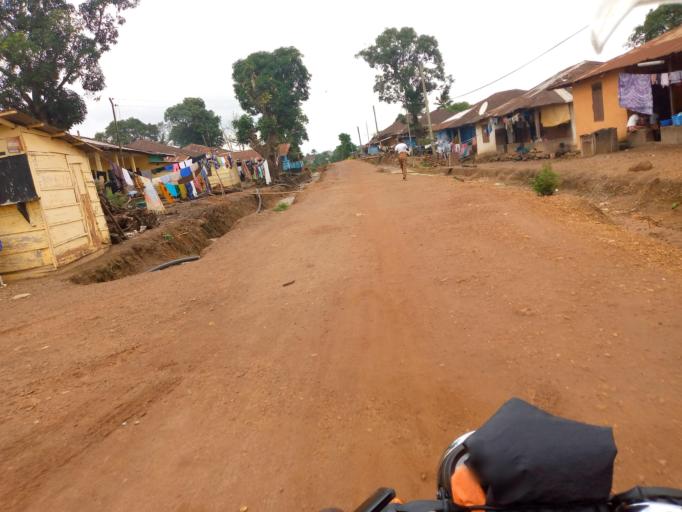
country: SL
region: Eastern Province
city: Kenema
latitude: 7.8735
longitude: -11.1867
